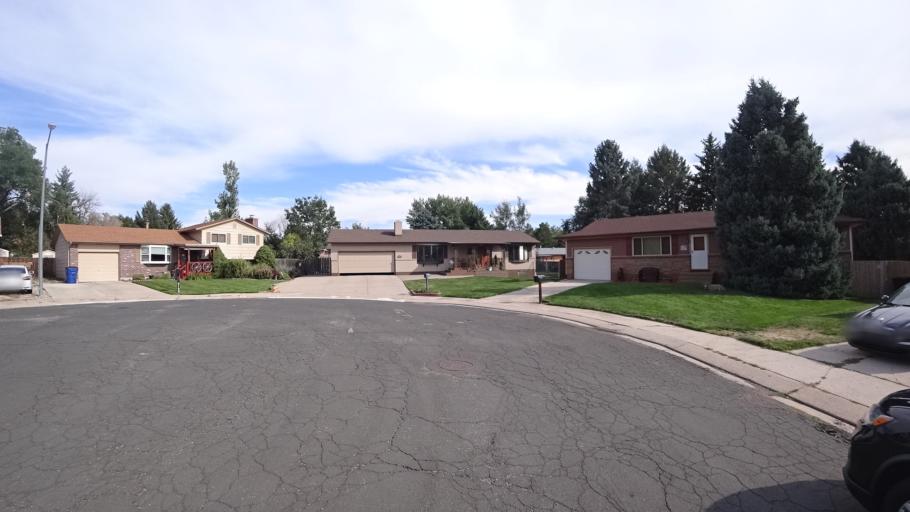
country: US
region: Colorado
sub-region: El Paso County
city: Cimarron Hills
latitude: 38.8982
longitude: -104.7667
